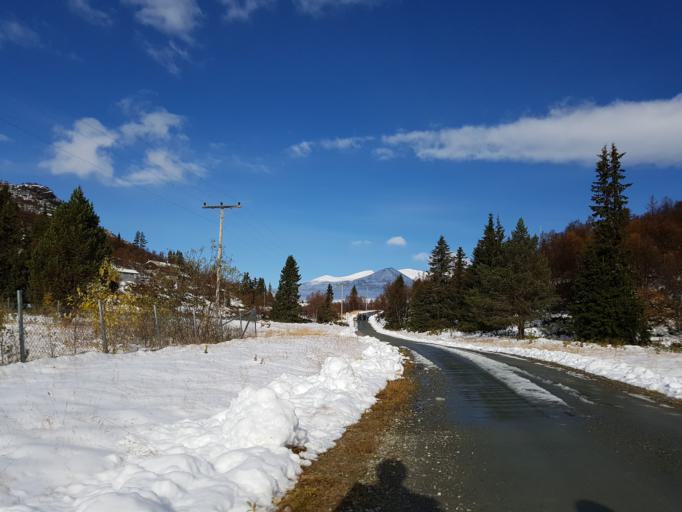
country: NO
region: Oppland
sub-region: Sel
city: Otta
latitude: 61.8174
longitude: 9.6775
